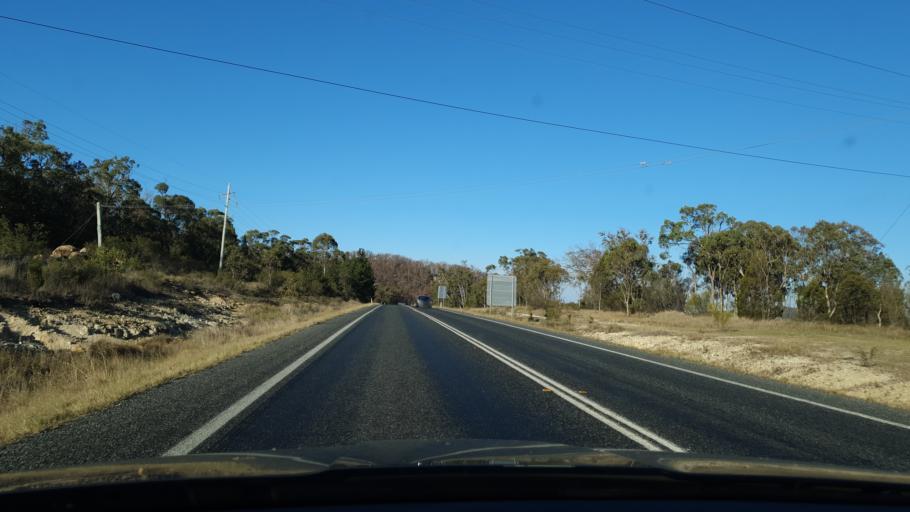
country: AU
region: Queensland
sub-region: Southern Downs
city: Stanthorpe
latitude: -28.6478
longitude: 151.9245
